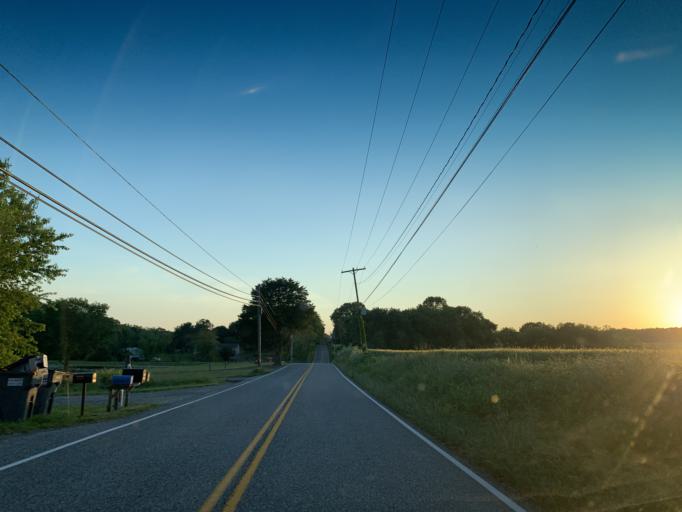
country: US
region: Maryland
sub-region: Cecil County
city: North East
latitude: 39.6423
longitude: -75.9818
